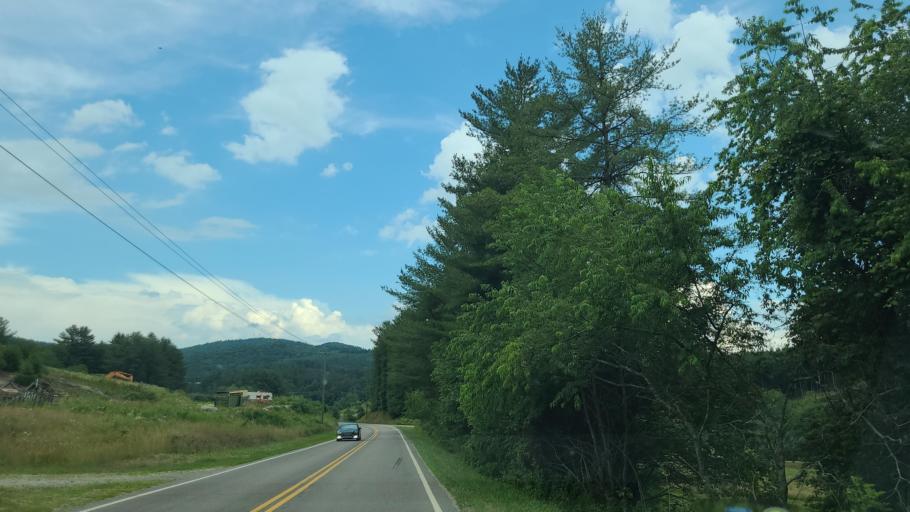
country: US
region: North Carolina
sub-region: Alleghany County
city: Sparta
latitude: 36.3967
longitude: -81.2521
